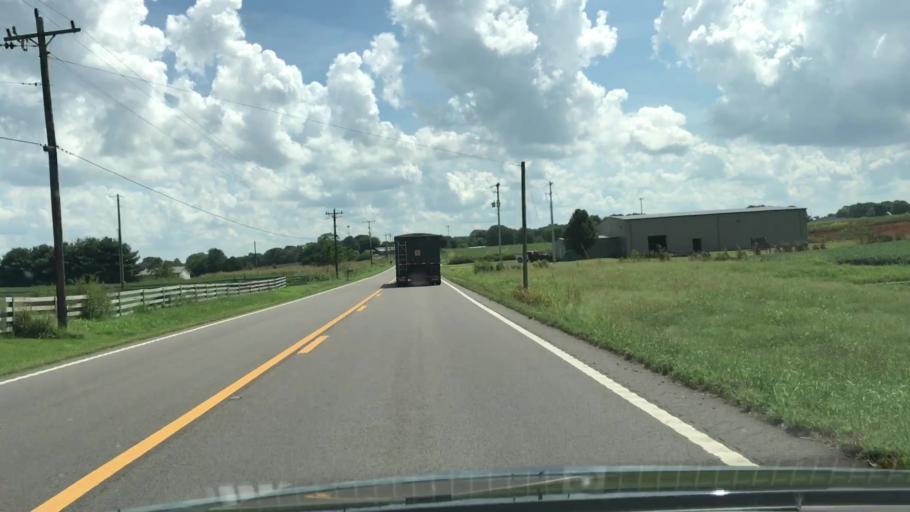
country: US
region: Tennessee
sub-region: Robertson County
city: Springfield
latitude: 36.6050
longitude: -86.9242
